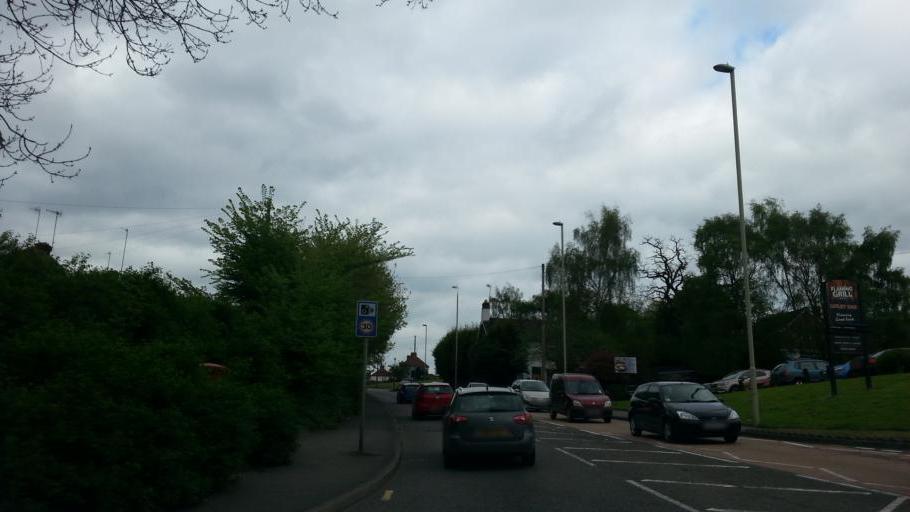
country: GB
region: England
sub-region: Sandwell
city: Cradley Heath
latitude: 52.4546
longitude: -2.0737
